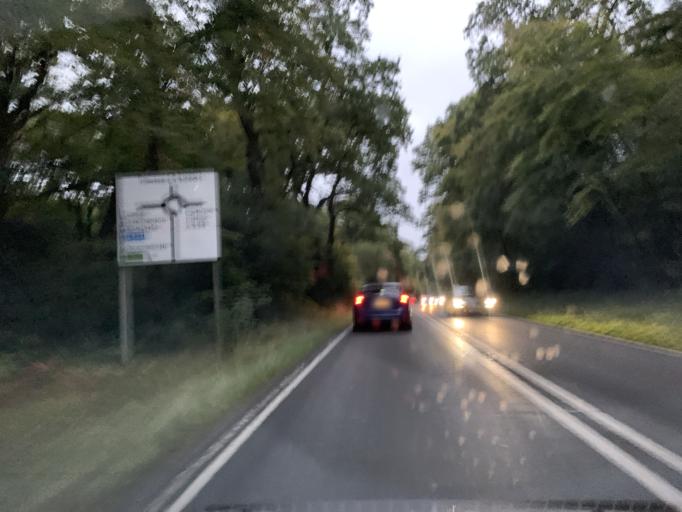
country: GB
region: England
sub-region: Hampshire
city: Cadnam
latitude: 50.9184
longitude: -1.5825
